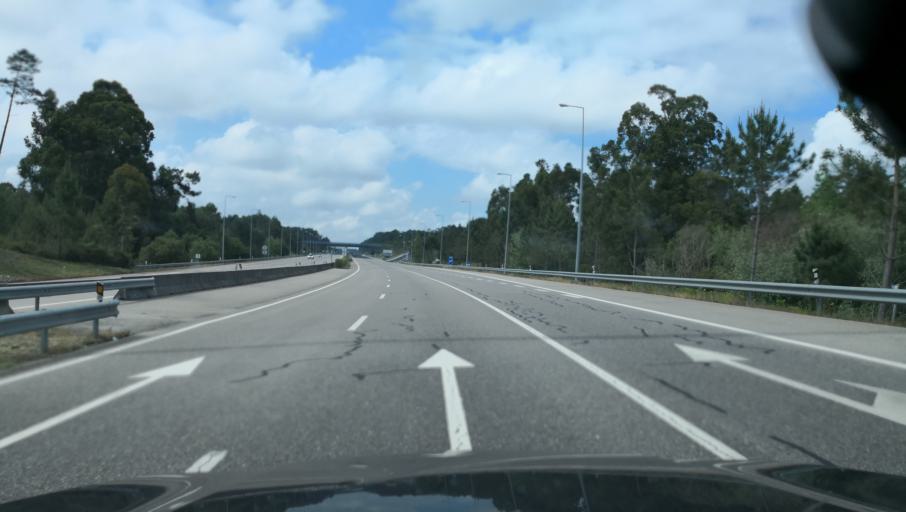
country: PT
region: Leiria
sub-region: Leiria
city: Maceira
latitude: 39.7178
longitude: -8.9126
